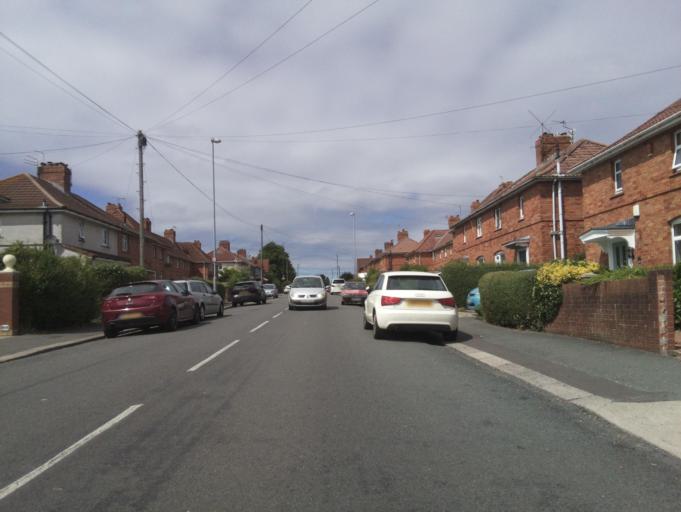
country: GB
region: England
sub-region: Bath and North East Somerset
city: Whitchurch
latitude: 51.4308
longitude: -2.5766
